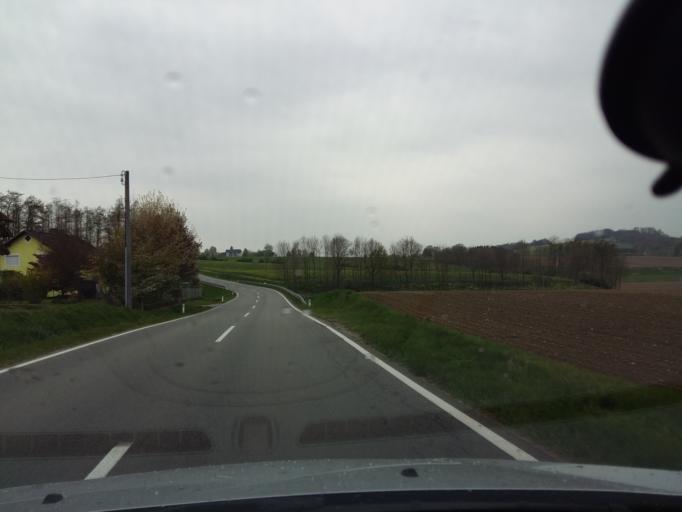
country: AT
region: Upper Austria
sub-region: Politischer Bezirk Scharding
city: Sankt Marienkirchen bei Schaerding
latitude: 48.4096
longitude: 13.5048
